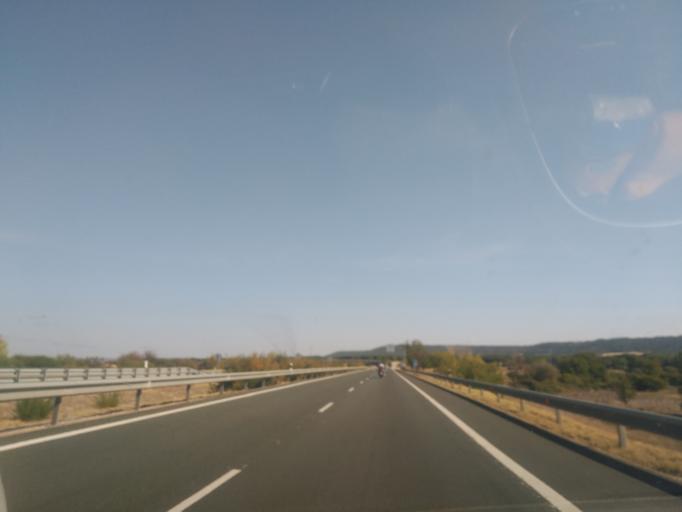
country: ES
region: Castille and Leon
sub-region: Provincia de Valladolid
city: Tudela de Duero
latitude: 41.5890
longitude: -4.5626
